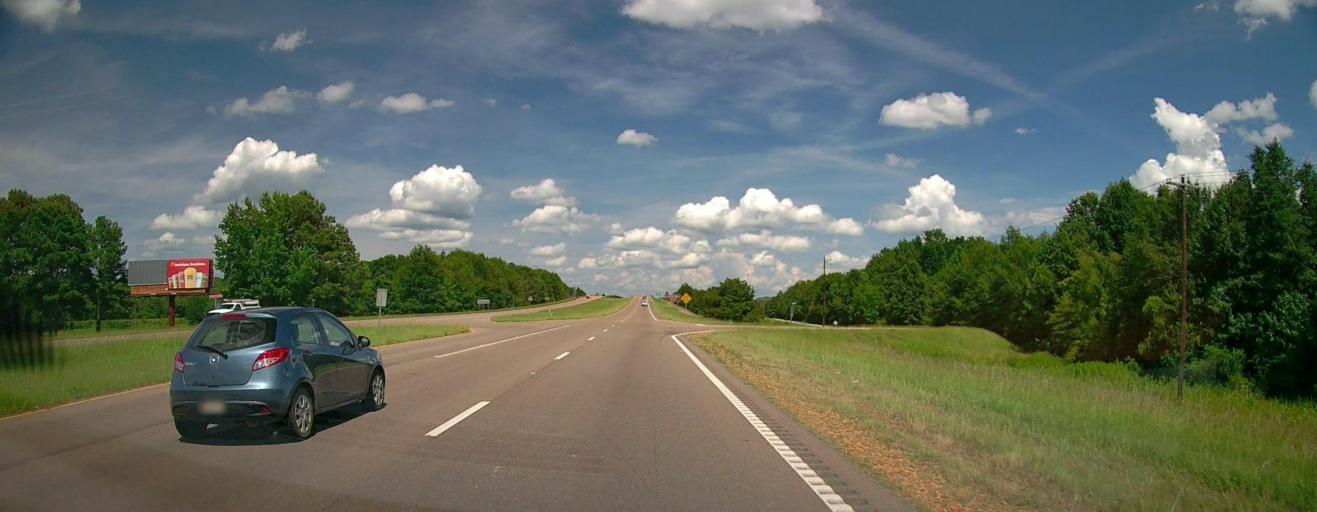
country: US
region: Mississippi
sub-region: Monroe County
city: Aberdeen
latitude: 33.8166
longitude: -88.5257
